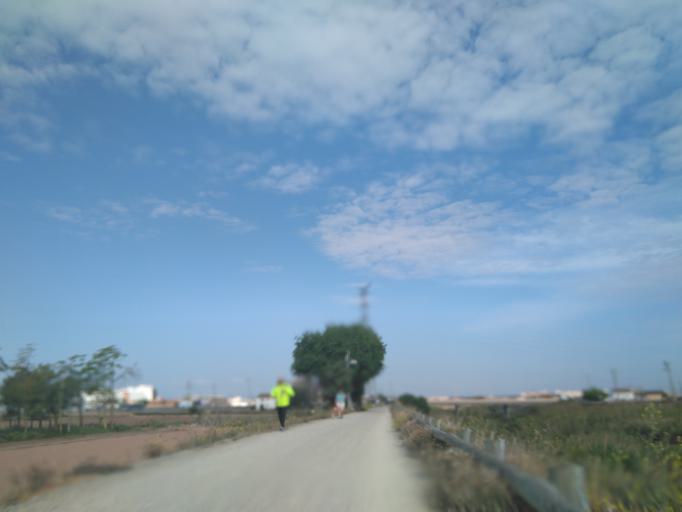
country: ES
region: Valencia
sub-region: Provincia de Valencia
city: Alboraya
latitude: 39.5040
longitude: -0.3417
